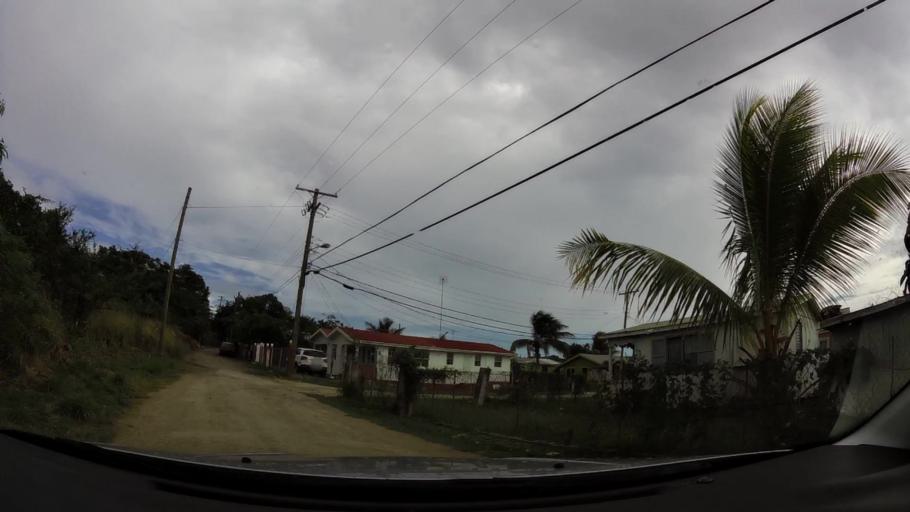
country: AG
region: Saint John
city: Potters Village
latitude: 17.0946
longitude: -61.8152
